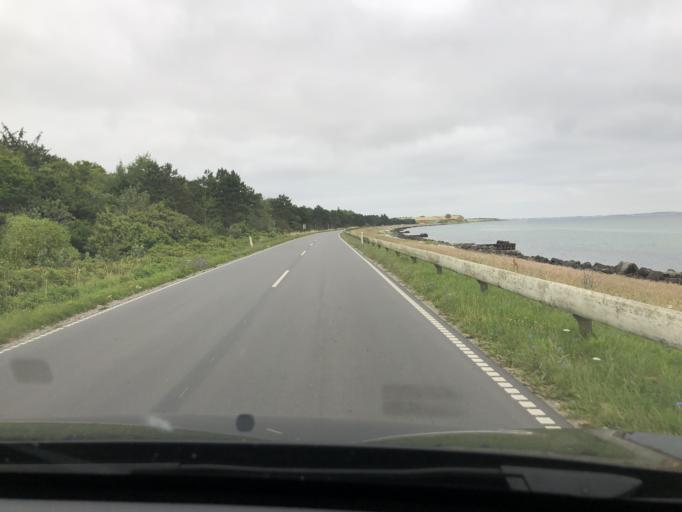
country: DK
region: South Denmark
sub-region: AEro Kommune
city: Marstal
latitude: 54.8391
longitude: 10.4562
